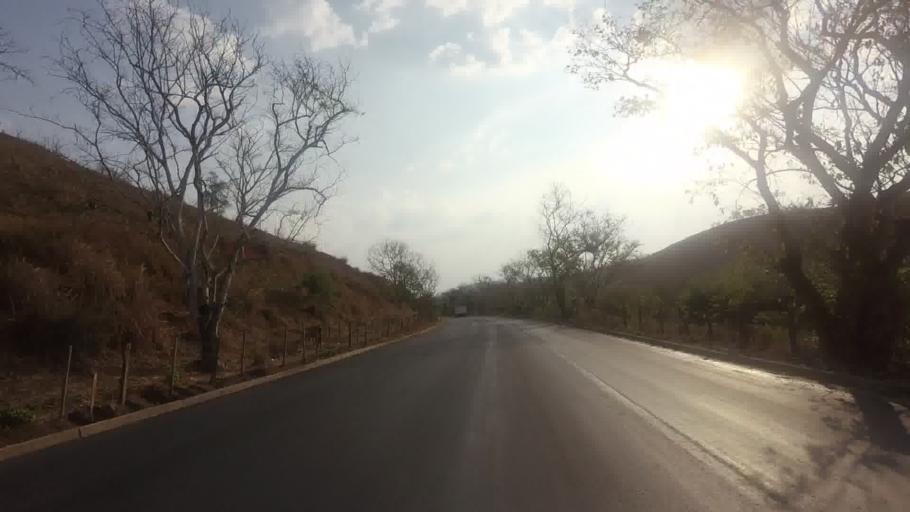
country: BR
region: Rio de Janeiro
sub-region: Itaperuna
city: Itaperuna
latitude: -21.3696
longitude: -41.9423
